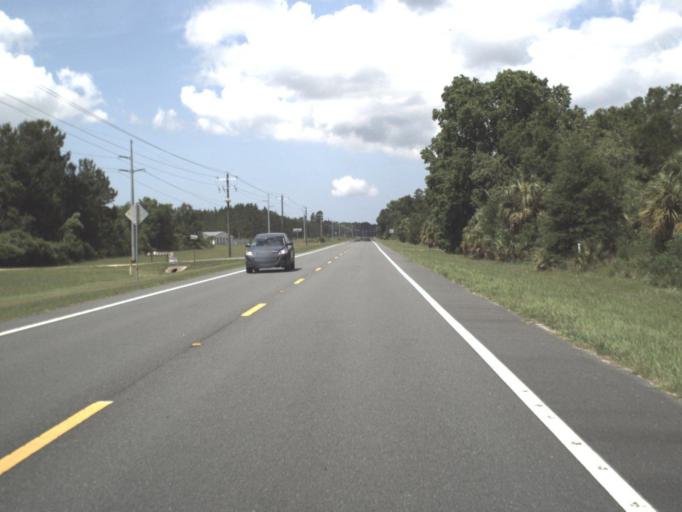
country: US
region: Florida
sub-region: Levy County
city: Chiefland
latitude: 29.2329
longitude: -82.9437
